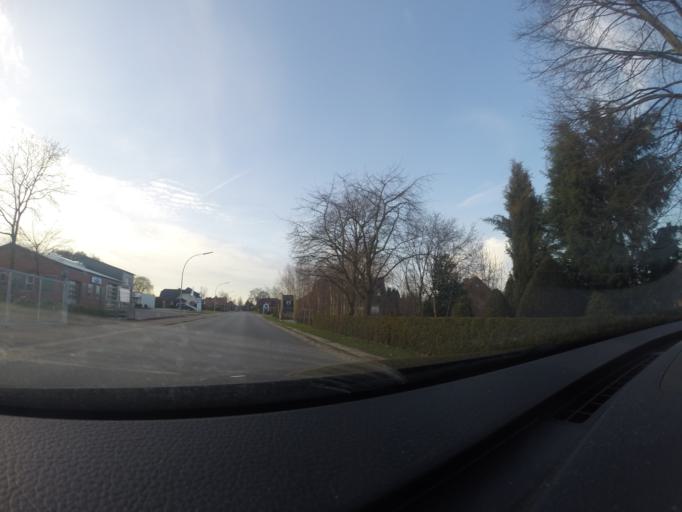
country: NL
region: Overijssel
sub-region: Gemeente Enschede
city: Enschede
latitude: 52.1224
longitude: 6.9193
